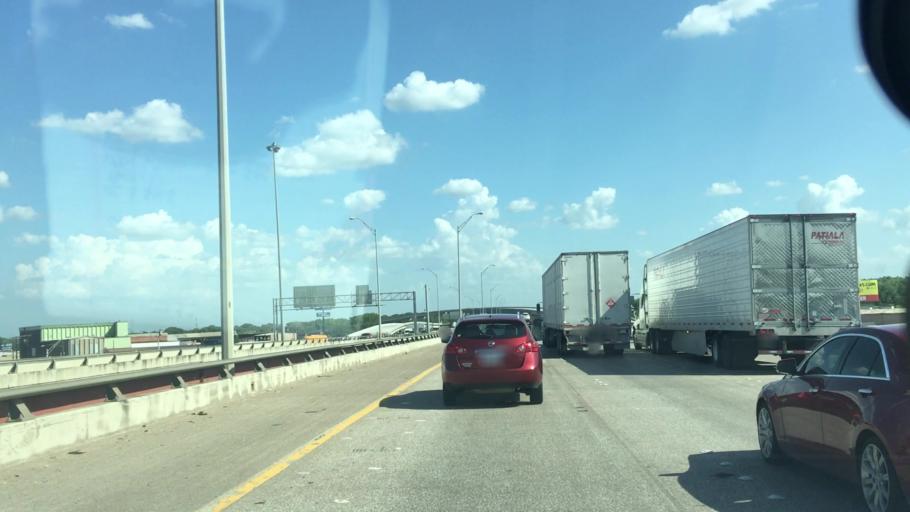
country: US
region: Texas
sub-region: Dallas County
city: Dallas
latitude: 32.7528
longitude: -96.7710
